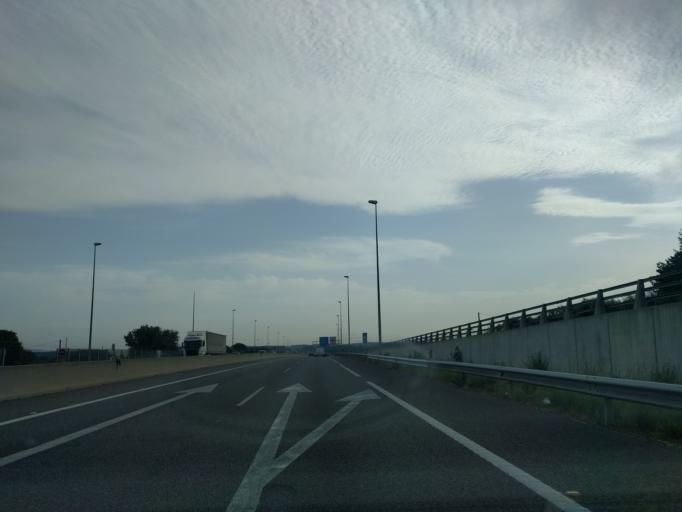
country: ES
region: Catalonia
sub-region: Provincia de Girona
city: Riudellots de la Selva
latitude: 41.8995
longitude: 2.7862
